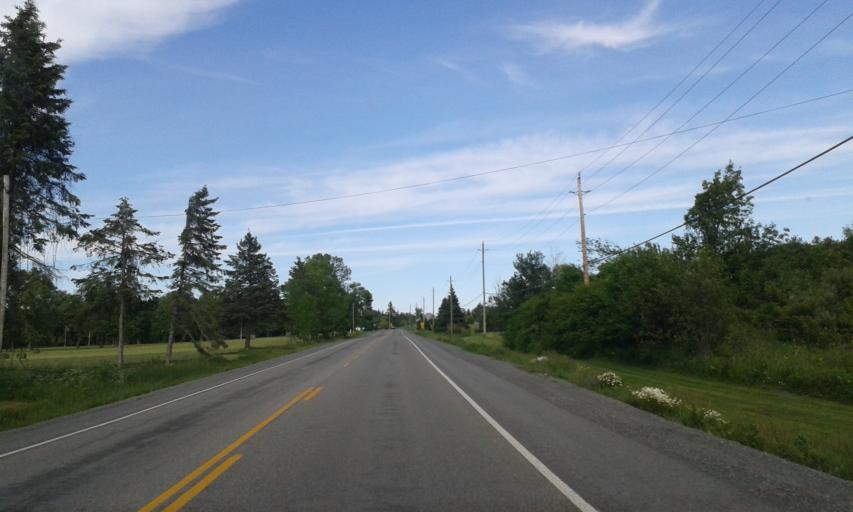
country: CA
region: Ontario
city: Cornwall
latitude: 45.1199
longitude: -74.5123
